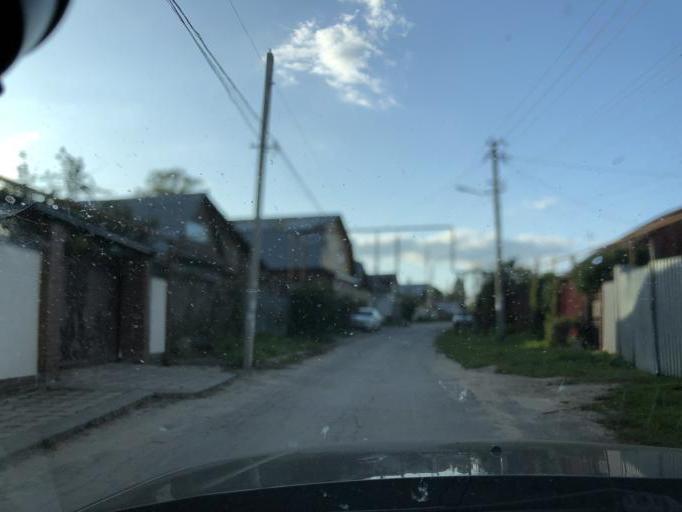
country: RU
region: Tula
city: Kosaya Gora
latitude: 54.1820
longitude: 37.5371
